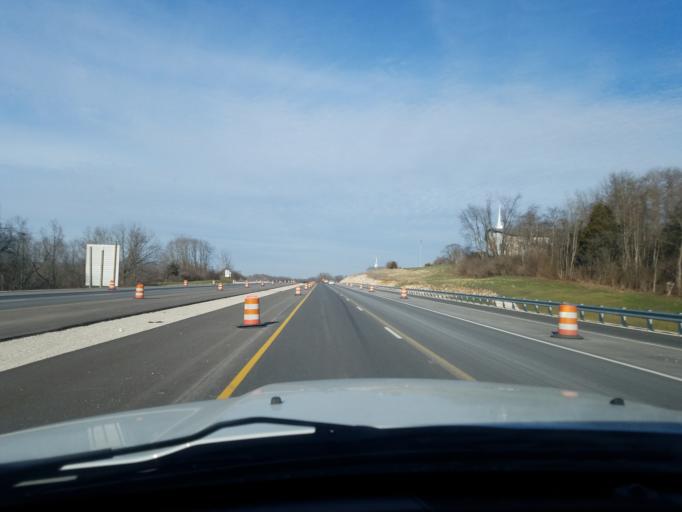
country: US
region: Indiana
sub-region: Monroe County
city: Bloomington
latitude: 39.2039
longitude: -86.5538
